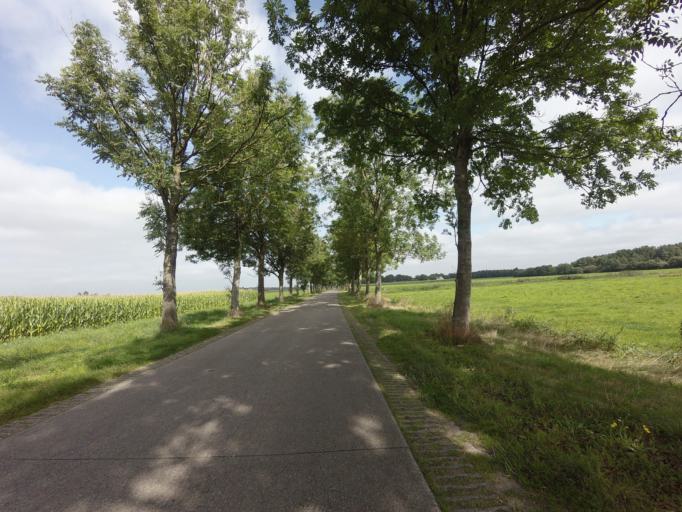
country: NL
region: Drenthe
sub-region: Gemeente Westerveld
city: Havelte
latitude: 52.8353
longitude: 6.2349
